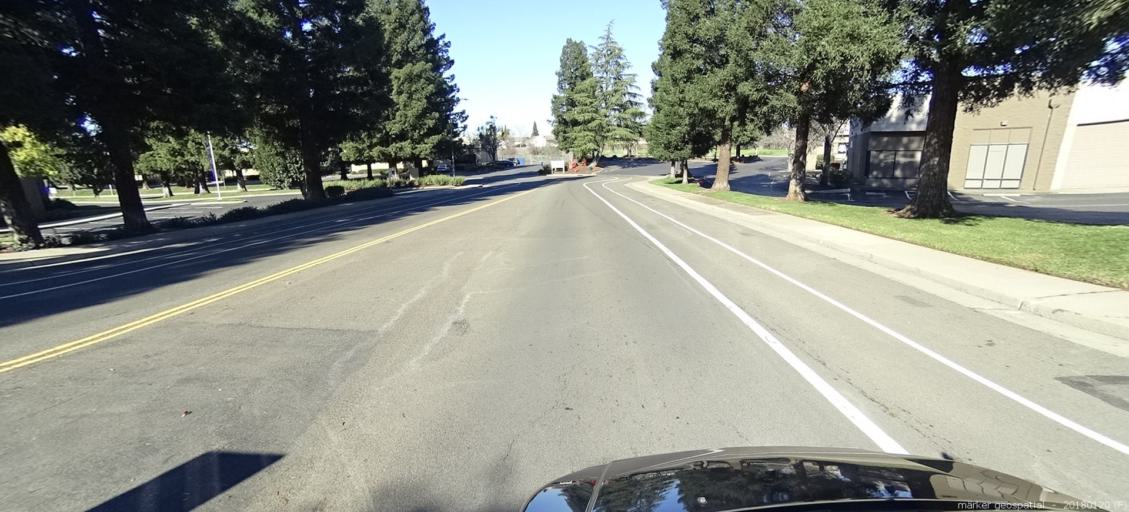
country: US
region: California
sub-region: Sacramento County
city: Rancho Cordova
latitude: 38.5656
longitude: -121.3108
